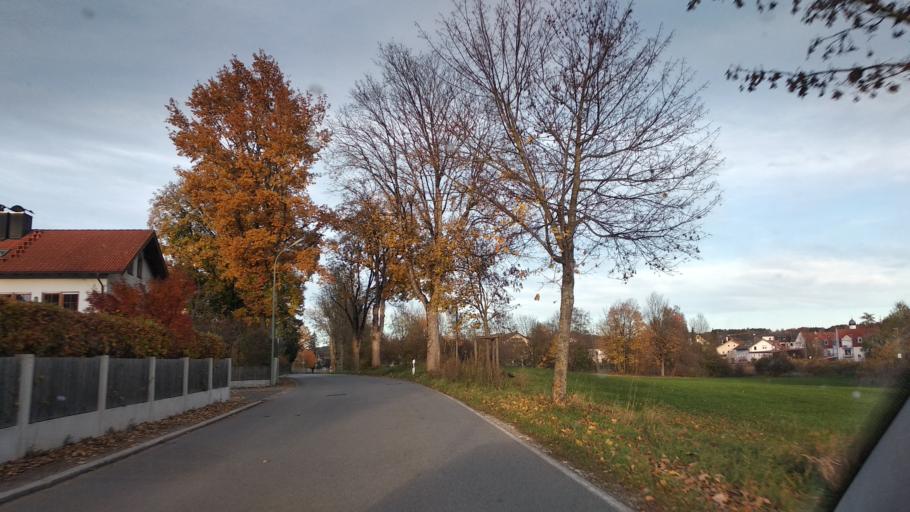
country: DE
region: Bavaria
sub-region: Upper Bavaria
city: Grafing bei Munchen
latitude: 48.0455
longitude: 11.9584
